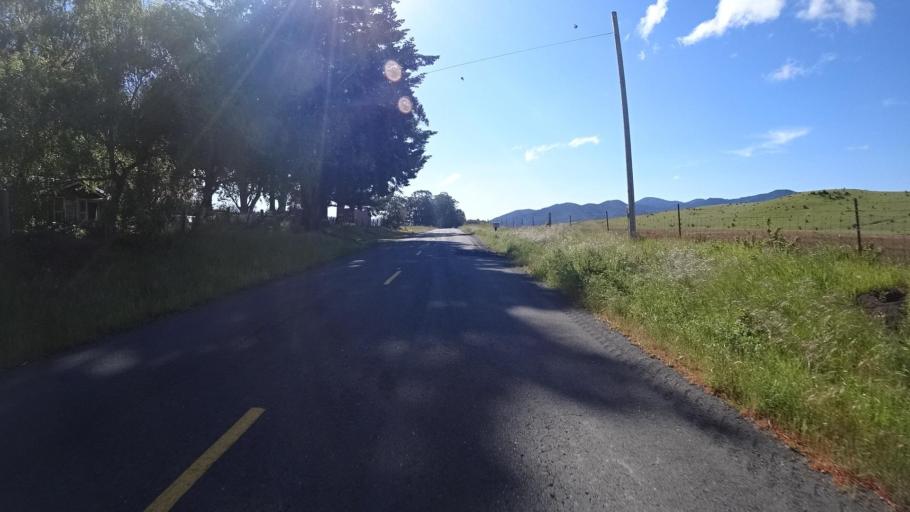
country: US
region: California
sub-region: Humboldt County
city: Ferndale
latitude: 40.3392
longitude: -124.3137
